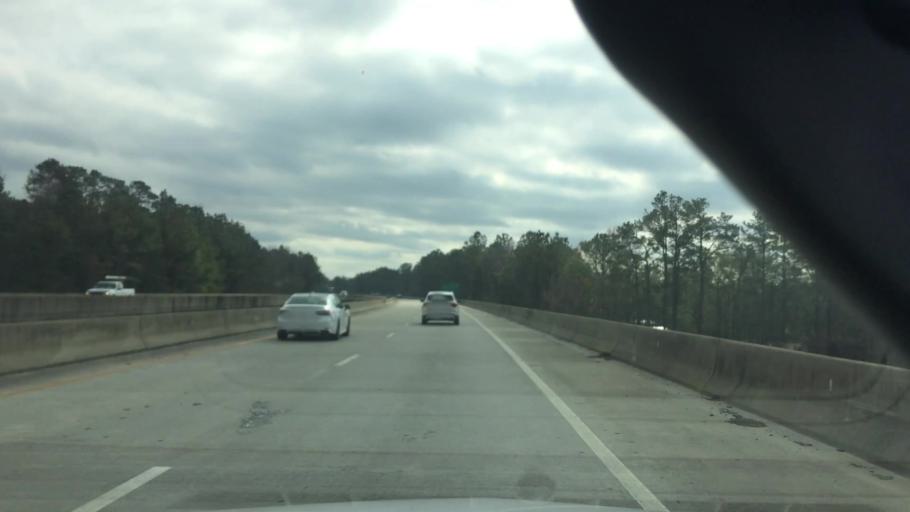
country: US
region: North Carolina
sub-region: New Hanover County
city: Castle Hayne
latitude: 34.3647
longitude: -77.8885
